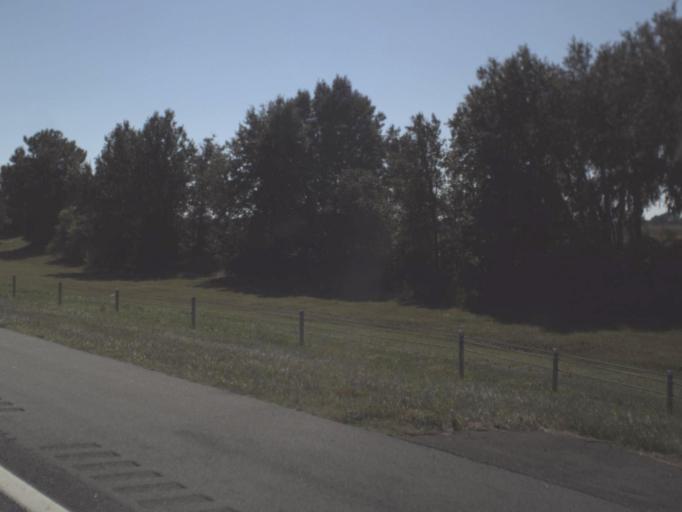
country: US
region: Florida
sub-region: Lake County
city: Hawthorne
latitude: 28.7449
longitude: -81.9278
